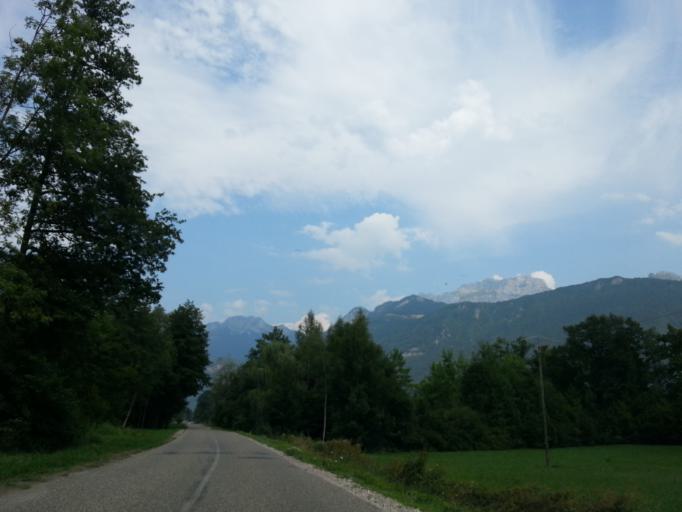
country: FR
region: Rhone-Alpes
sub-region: Departement de la Haute-Savoie
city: Doussard
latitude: 45.7833
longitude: 6.2084
